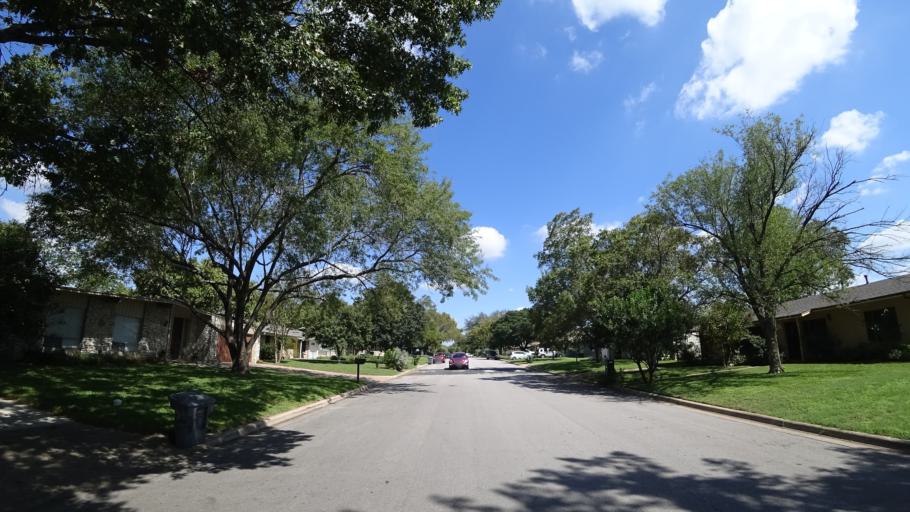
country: US
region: Texas
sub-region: Travis County
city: Austin
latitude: 30.3325
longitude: -97.7090
